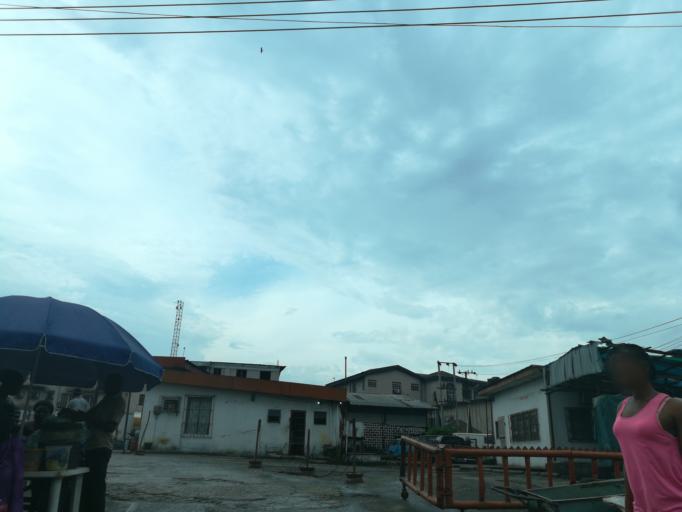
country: NG
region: Rivers
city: Port Harcourt
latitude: 4.7925
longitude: 7.0010
